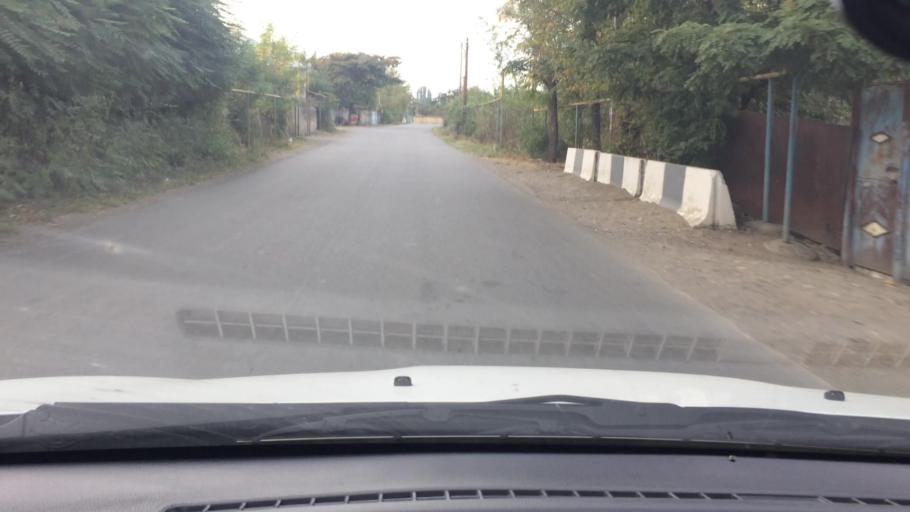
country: GE
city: Naghvarevi
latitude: 41.3511
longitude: 44.8644
